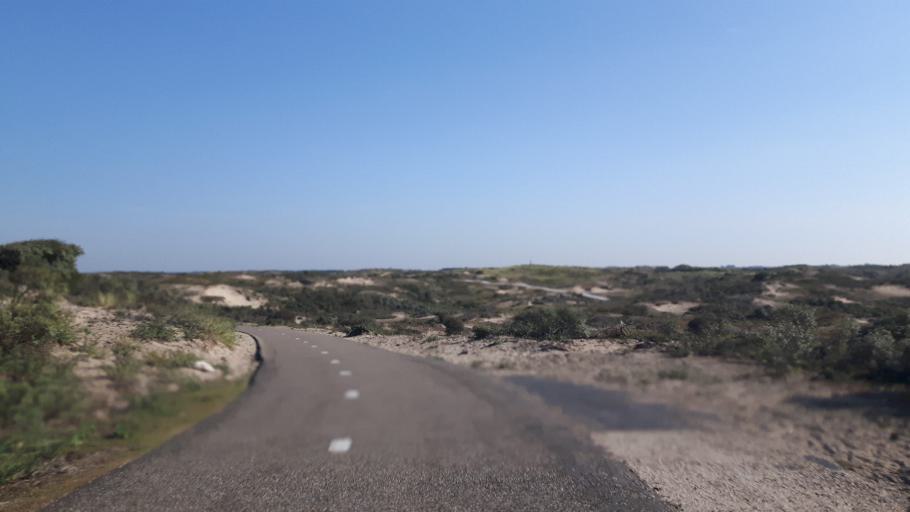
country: NL
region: South Holland
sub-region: Gemeente Noordwijkerhout
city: Noordwijkerhout
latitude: 52.3095
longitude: 4.4859
